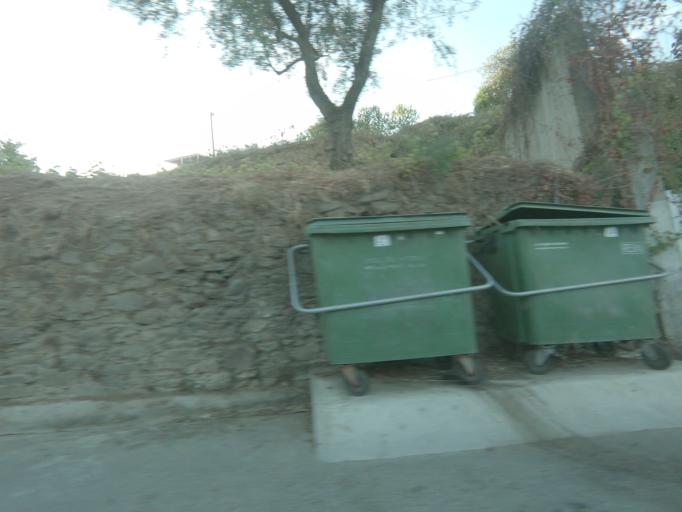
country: PT
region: Vila Real
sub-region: Peso da Regua
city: Godim
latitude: 41.1644
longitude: -7.8102
